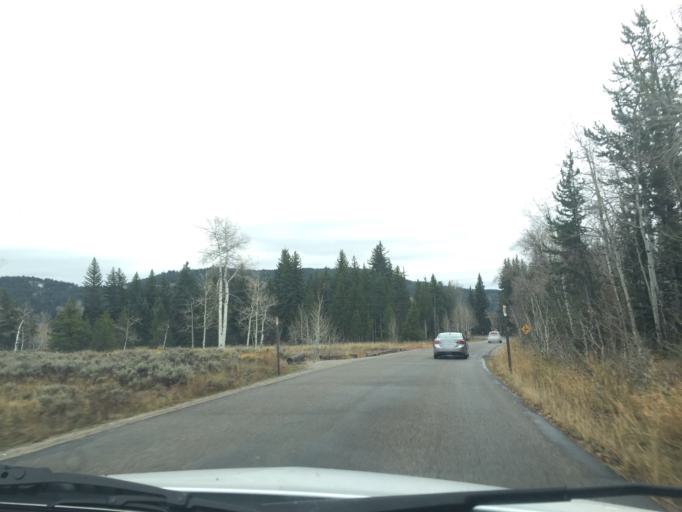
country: US
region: Wyoming
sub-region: Teton County
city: Moose Wilson Road
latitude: 43.6577
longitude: -110.7220
